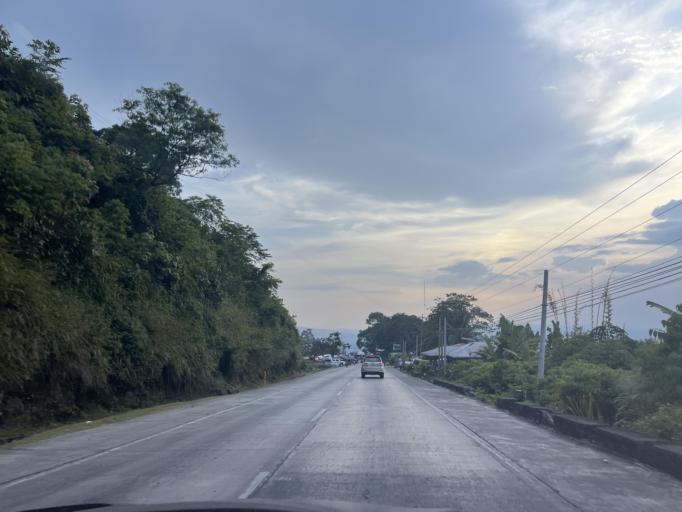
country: PH
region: Northern Mindanao
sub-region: Province of Bukidnon
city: Dalorong
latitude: 7.6040
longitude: 125.1504
